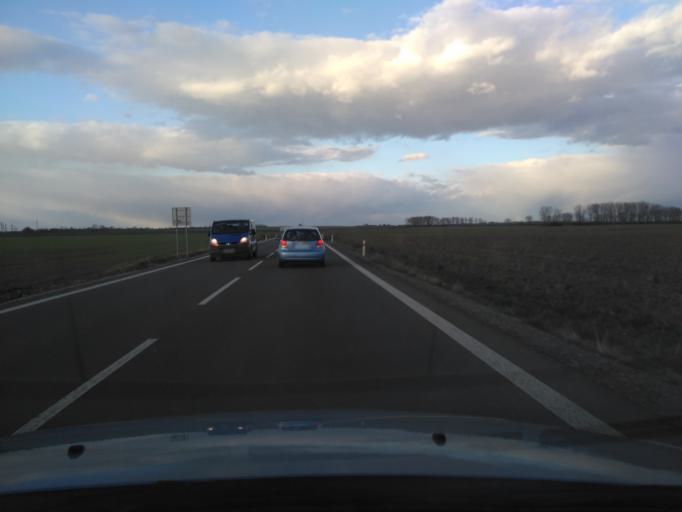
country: SK
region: Kosicky
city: Trebisov
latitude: 48.5504
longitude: 21.6932
